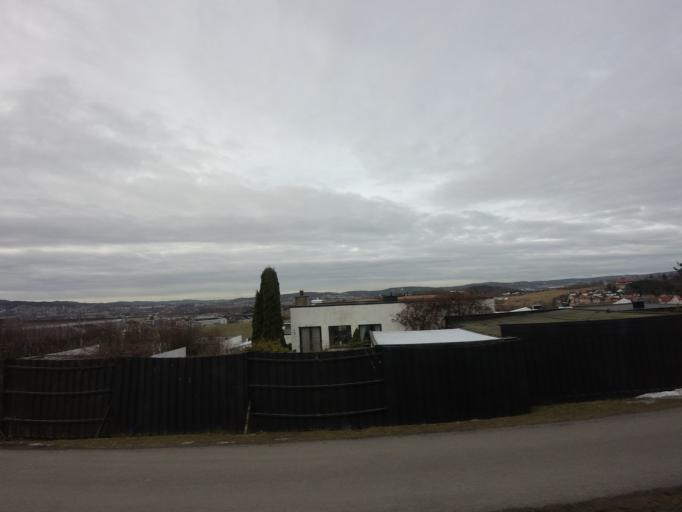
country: NO
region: Akershus
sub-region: Skedsmo
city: Lillestrom
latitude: 59.9817
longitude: 11.0520
